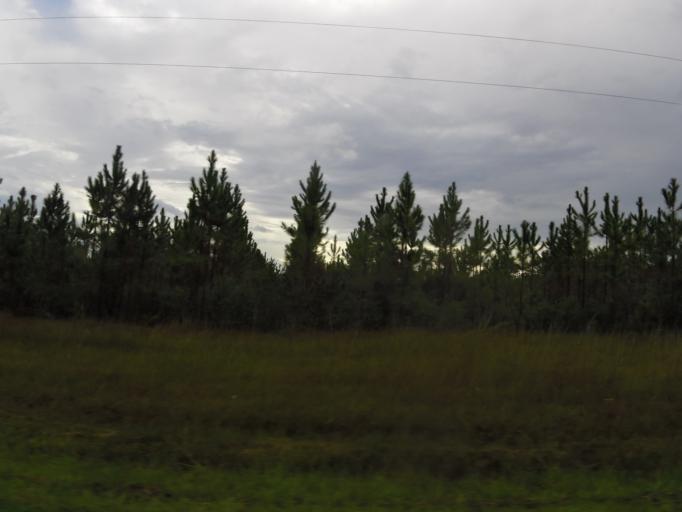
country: US
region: Florida
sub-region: Duval County
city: Baldwin
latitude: 30.3997
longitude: -82.0063
